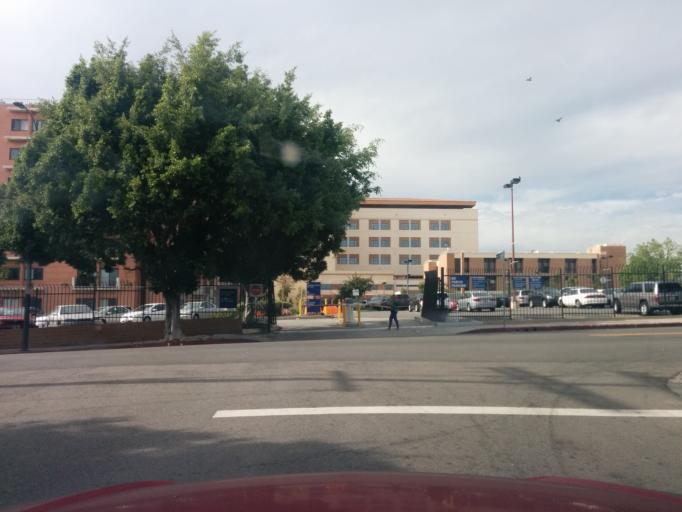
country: US
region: California
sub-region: Los Angeles County
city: Boyle Heights
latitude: 34.0483
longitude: -118.2161
